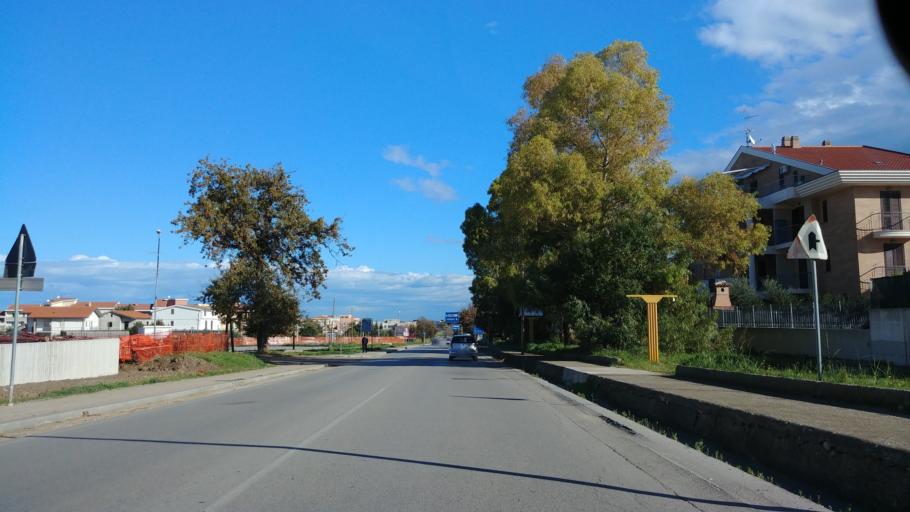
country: IT
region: Molise
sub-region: Provincia di Campobasso
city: Termoli
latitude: 41.9914
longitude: 14.9755
